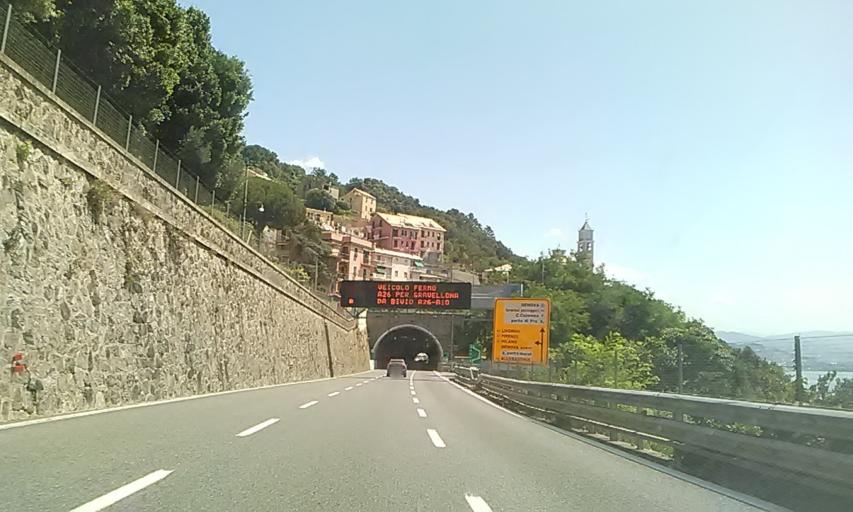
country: IT
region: Liguria
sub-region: Provincia di Genova
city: Mele
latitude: 44.4223
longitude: 8.7303
